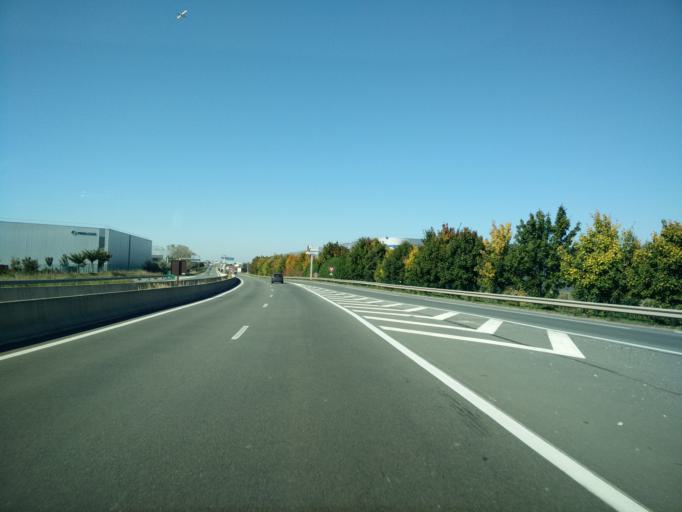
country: FR
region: Ile-de-France
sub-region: Departement de Seine-et-Marne
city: Mitry-Mory
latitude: 48.9934
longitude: 2.6539
